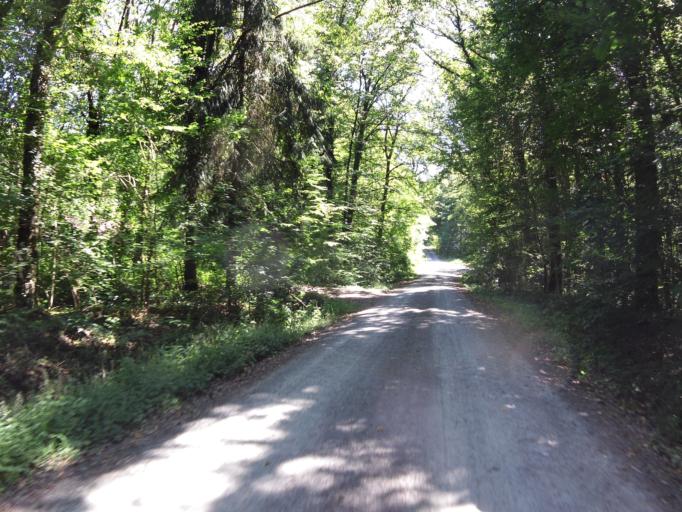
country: DE
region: Bavaria
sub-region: Regierungsbezirk Unterfranken
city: Kleinrinderfeld
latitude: 49.7170
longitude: 9.8700
